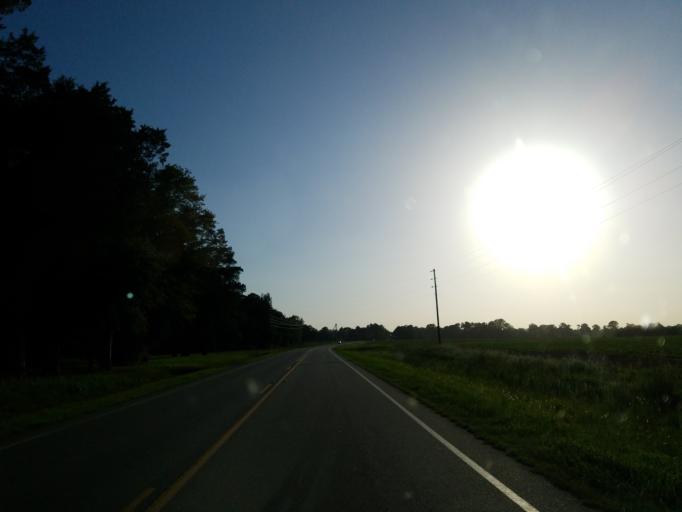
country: US
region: Georgia
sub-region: Irwin County
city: Ocilla
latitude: 31.6454
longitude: -83.3443
